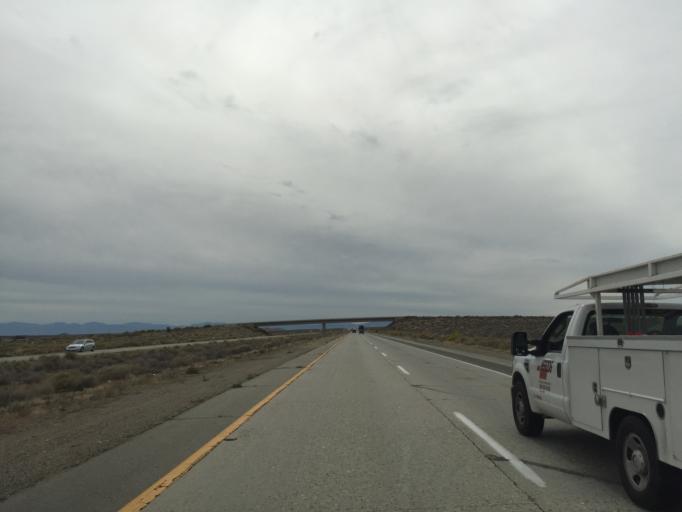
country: US
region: California
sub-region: Kern County
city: Rosamond
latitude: 34.9548
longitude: -118.1611
